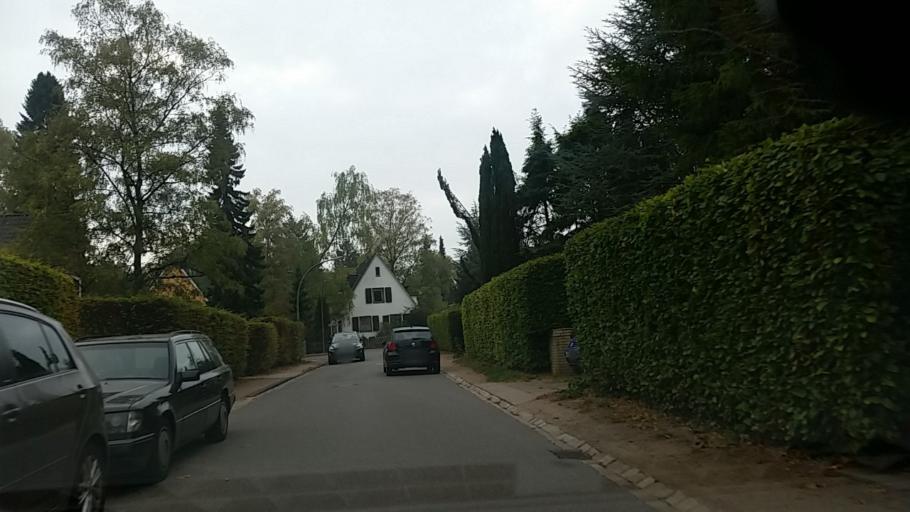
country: DE
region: Schleswig-Holstein
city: Halstenbek
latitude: 53.5742
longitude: 9.8092
